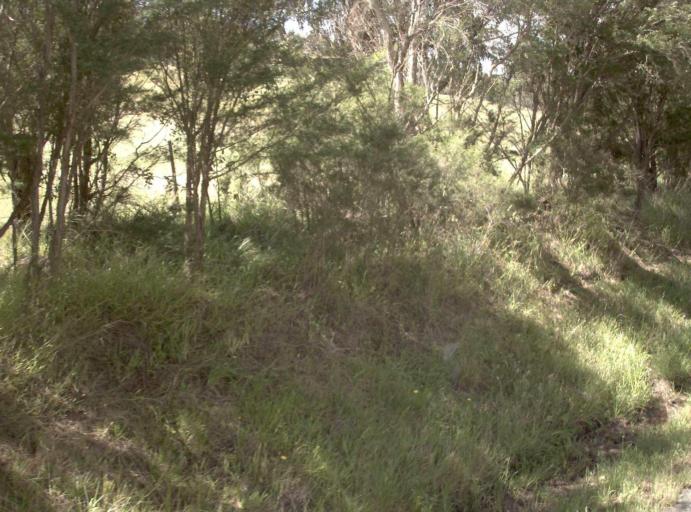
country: AU
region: Victoria
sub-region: Latrobe
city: Morwell
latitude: -38.1551
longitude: 146.4322
